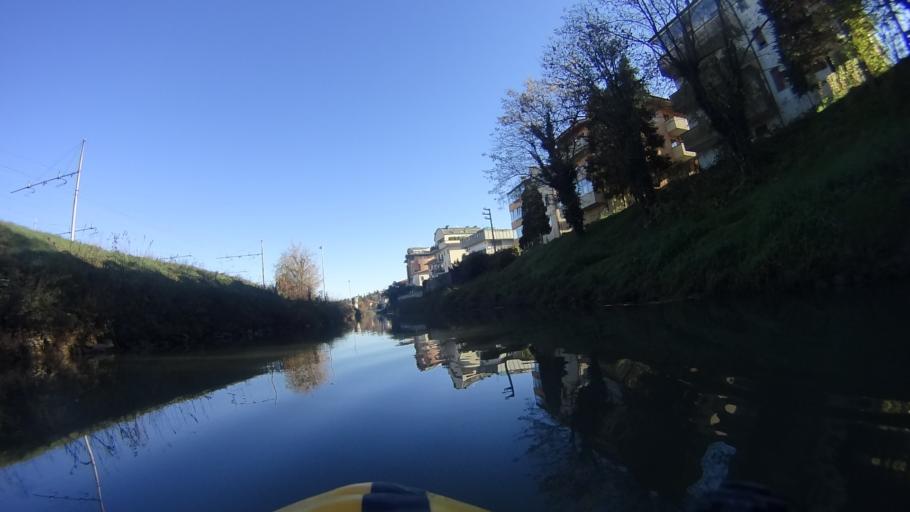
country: IT
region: Veneto
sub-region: Provincia di Vicenza
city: Vicenza
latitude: 45.5403
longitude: 11.5338
